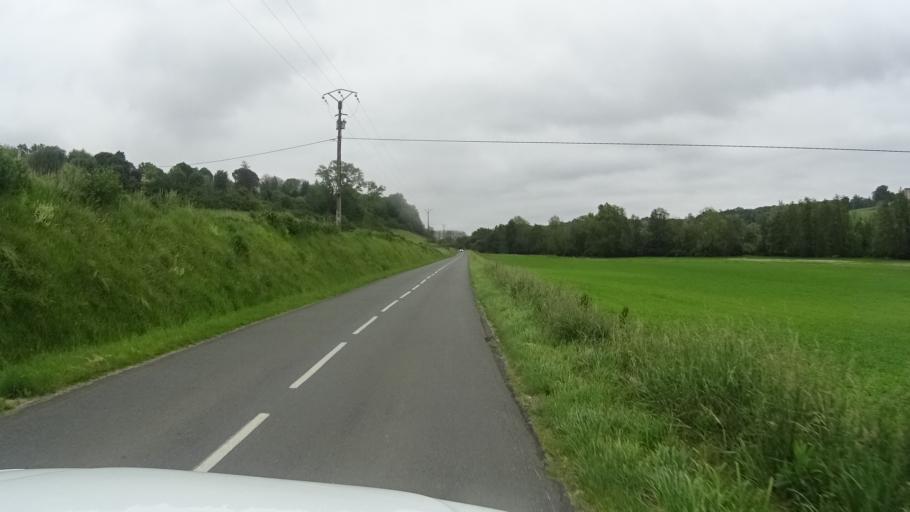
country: FR
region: Aquitaine
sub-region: Departement de la Dordogne
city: Sourzac
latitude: 45.0173
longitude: 0.4263
